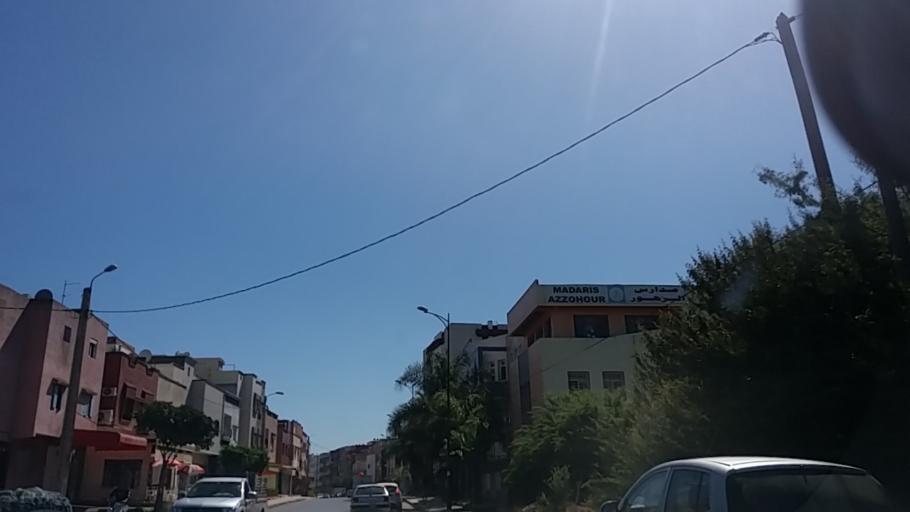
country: MA
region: Gharb-Chrarda-Beni Hssen
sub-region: Kenitra Province
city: Kenitra
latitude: 34.2468
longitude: -6.6112
